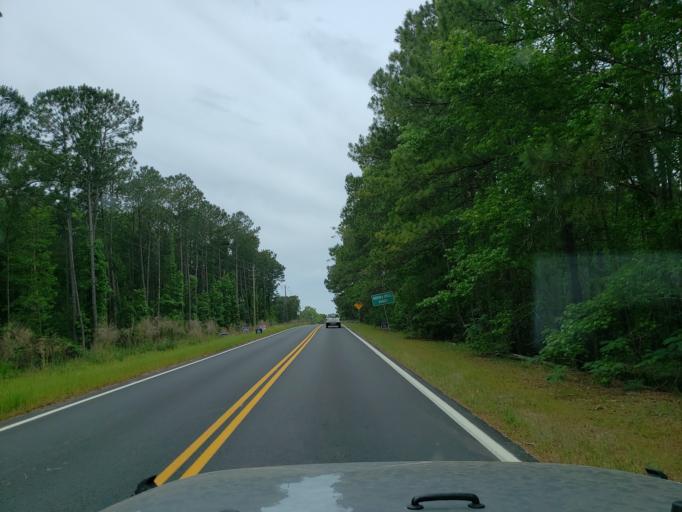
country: US
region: Georgia
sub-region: Chatham County
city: Port Wentworth
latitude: 32.1802
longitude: -81.2017
